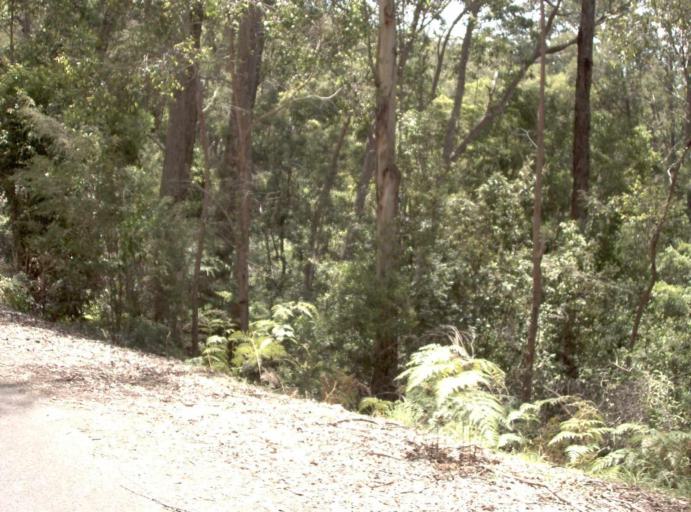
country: AU
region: New South Wales
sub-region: Bombala
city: Bombala
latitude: -37.5202
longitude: 148.9300
